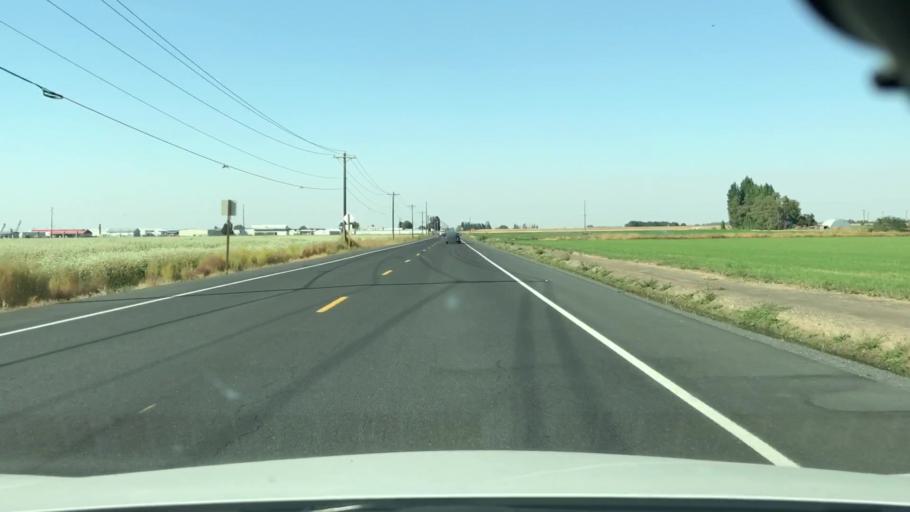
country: US
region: Washington
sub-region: Grant County
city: Moses Lake
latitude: 47.1264
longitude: -119.2358
